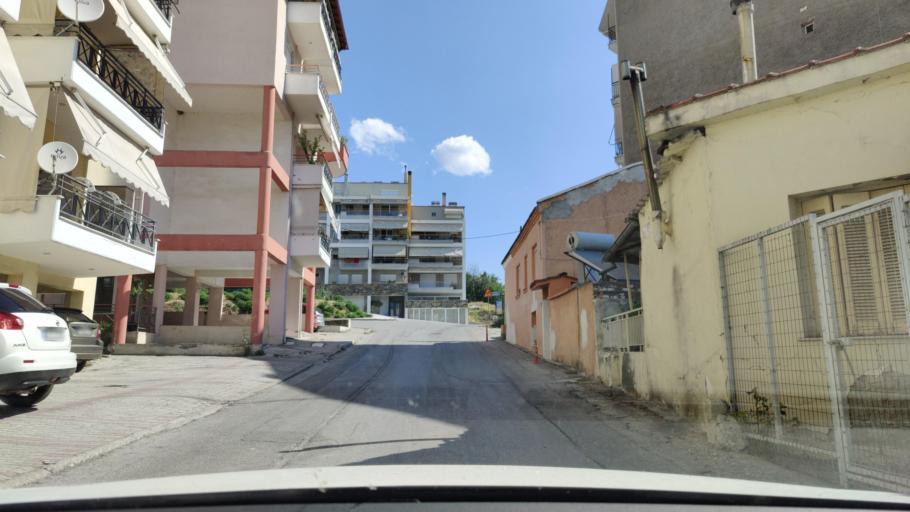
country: GR
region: Central Macedonia
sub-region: Nomos Serron
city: Serres
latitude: 41.0869
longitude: 23.5347
